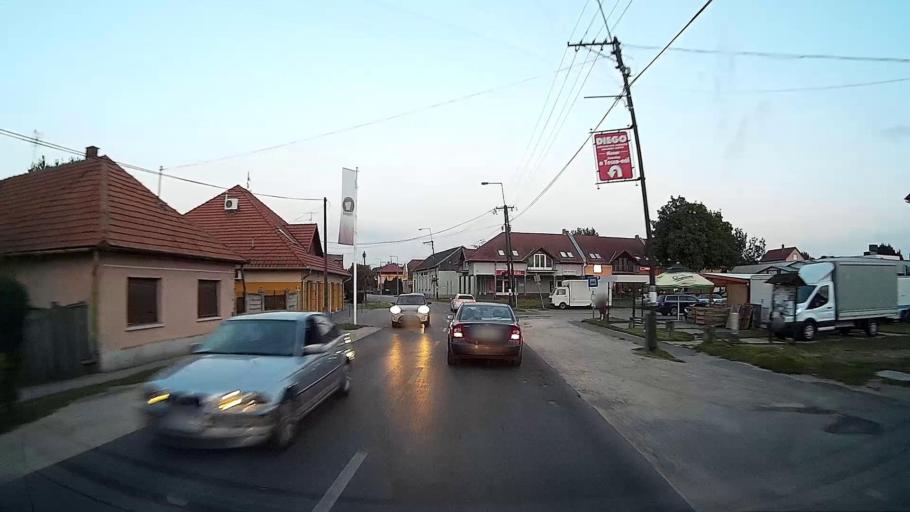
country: HU
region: Pest
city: Albertirsa
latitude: 47.2457
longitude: 19.6151
